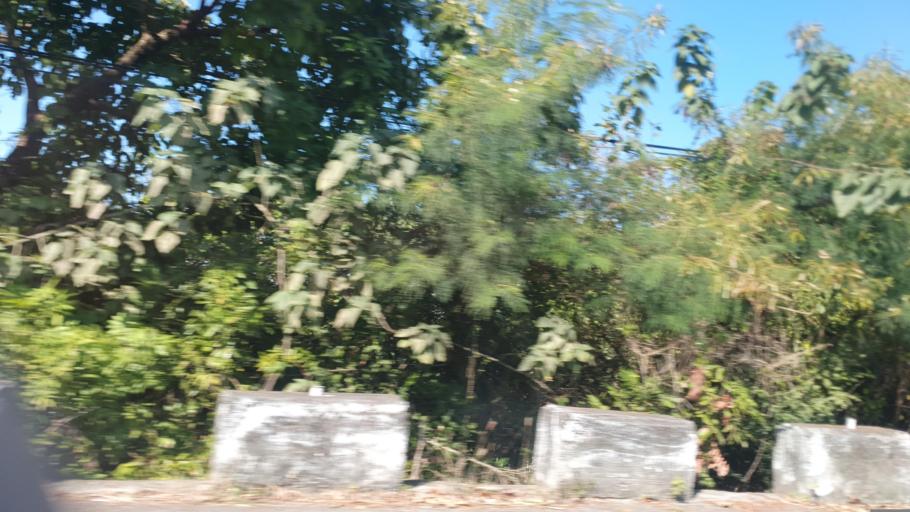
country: TW
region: Taiwan
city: Yujing
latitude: 23.0382
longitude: 120.3580
